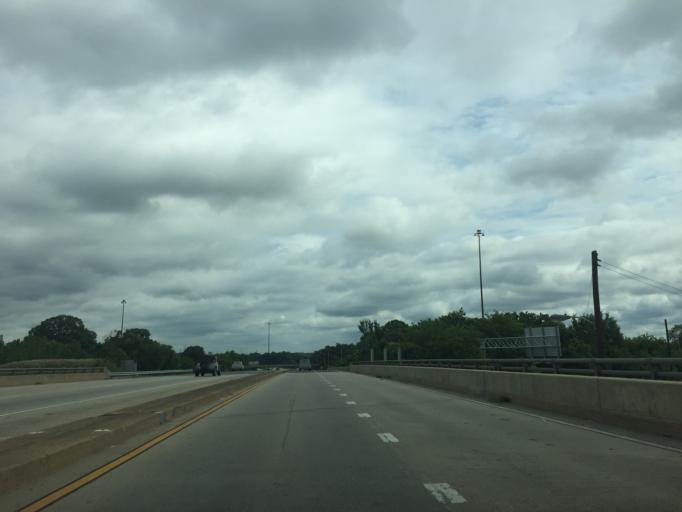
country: US
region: Maryland
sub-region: Baltimore County
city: Rosedale
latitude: 39.2971
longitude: -76.5026
